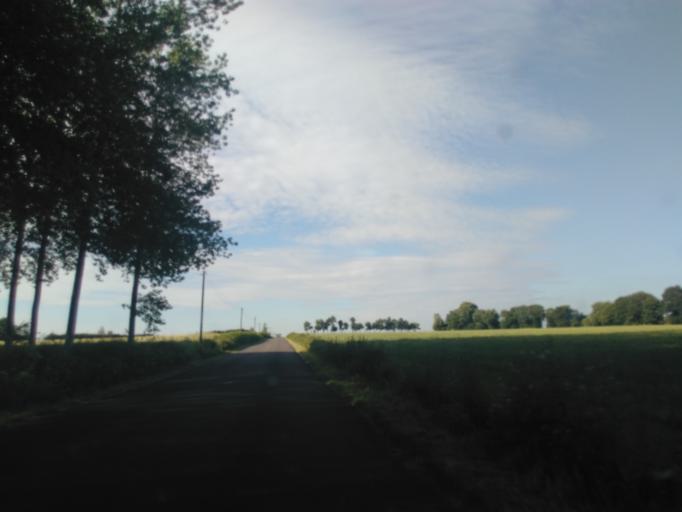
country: FR
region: Brittany
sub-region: Departement d'Ille-et-Vilaine
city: Pleumeleuc
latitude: 48.1917
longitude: -1.9102
